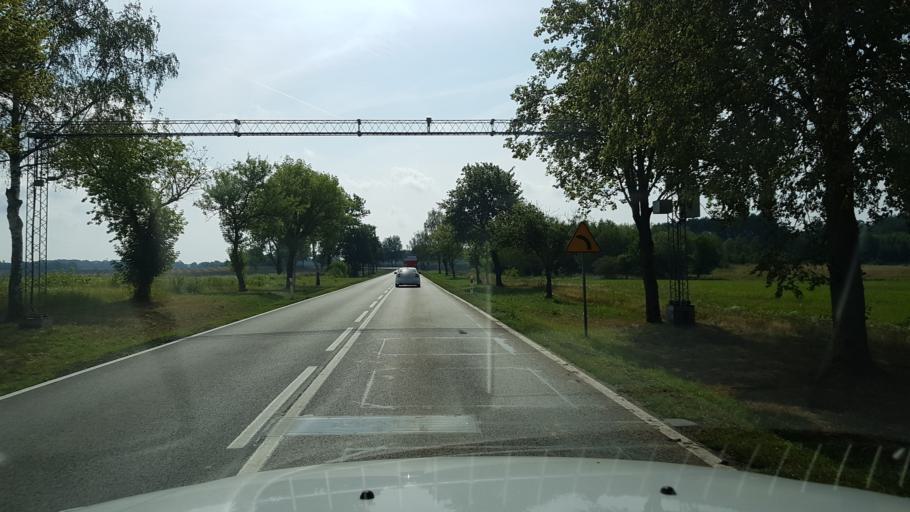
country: PL
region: West Pomeranian Voivodeship
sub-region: Powiat walecki
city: Walcz
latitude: 53.3229
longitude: 16.3133
